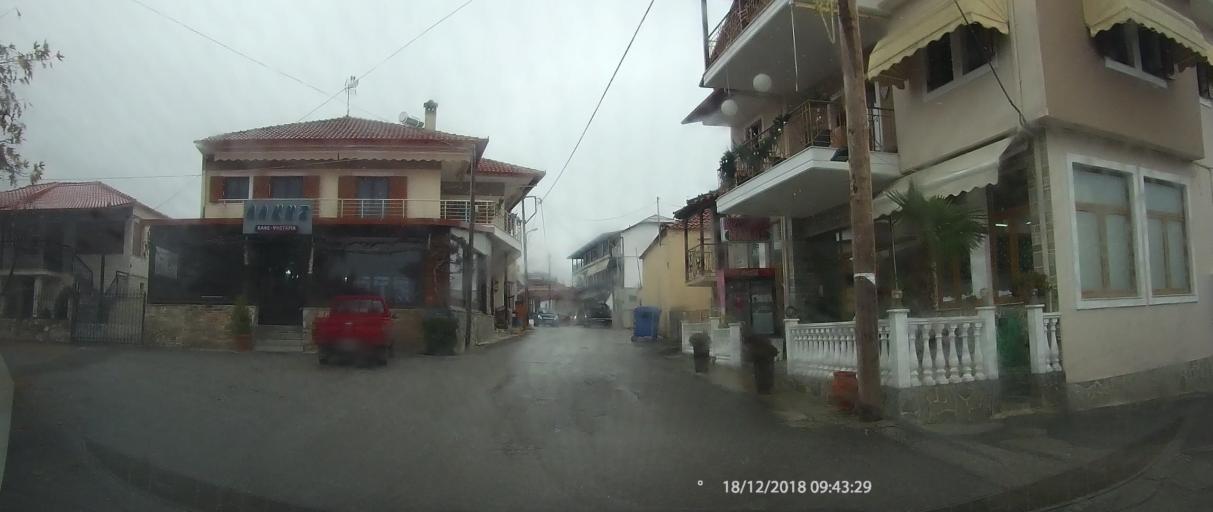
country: GR
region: Thessaly
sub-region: Nomos Larisis
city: Livadi
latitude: 40.0230
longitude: 22.2415
